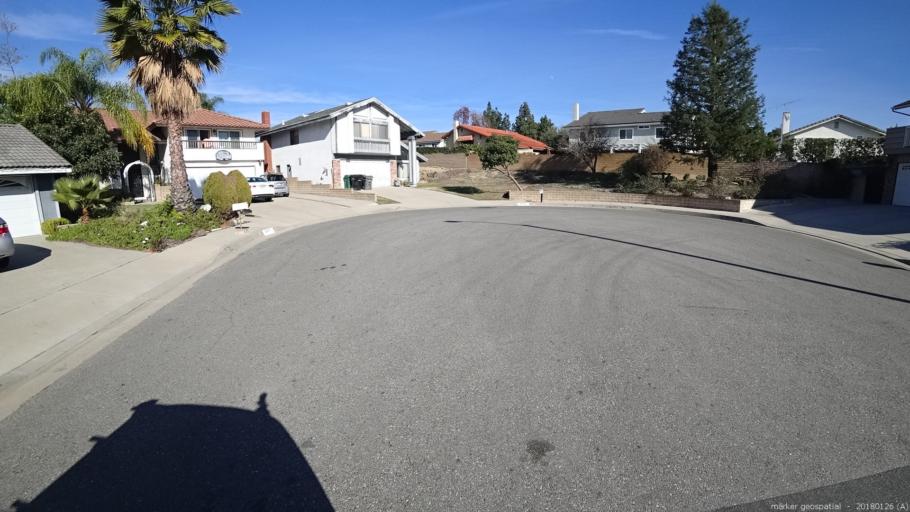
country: US
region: California
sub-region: Los Angeles County
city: Diamond Bar
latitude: 33.9979
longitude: -117.8081
